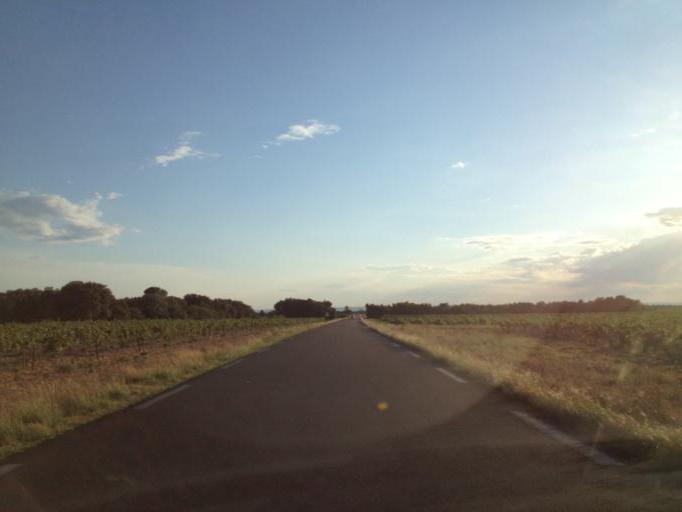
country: FR
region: Provence-Alpes-Cote d'Azur
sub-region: Departement du Vaucluse
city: Violes
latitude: 44.1712
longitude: 4.9278
